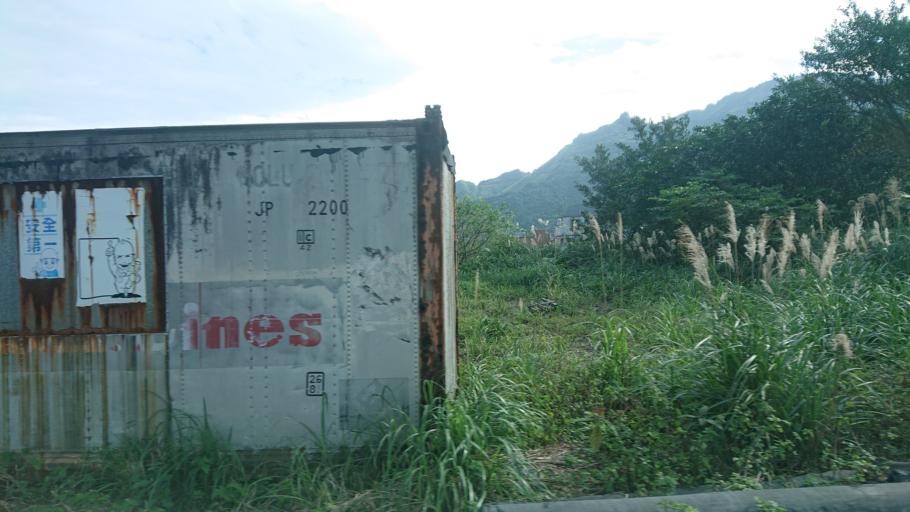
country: TW
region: Taiwan
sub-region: Keelung
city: Keelung
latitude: 25.1082
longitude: 121.8495
